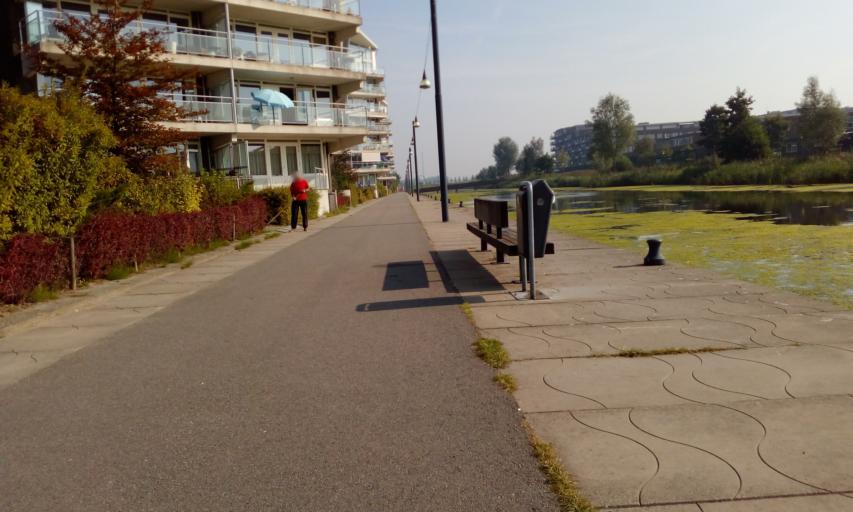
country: NL
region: South Holland
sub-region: Gemeente Rijnwoude
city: Benthuizen
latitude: 52.0643
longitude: 4.5432
